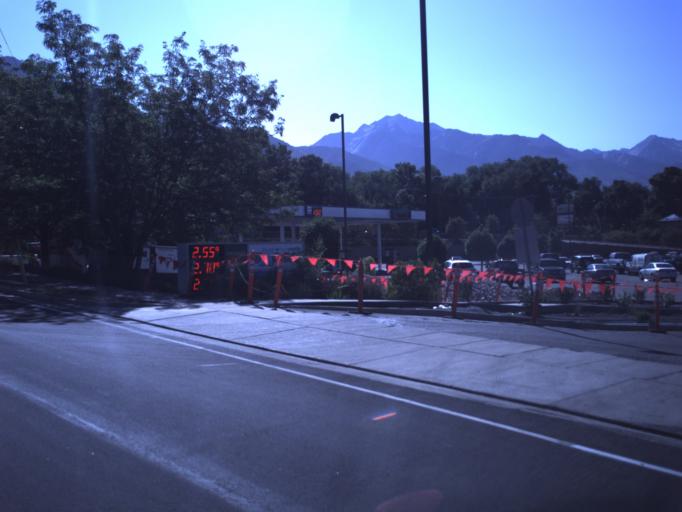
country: US
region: Utah
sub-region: Salt Lake County
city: Holladay
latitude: 40.6742
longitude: -111.8427
